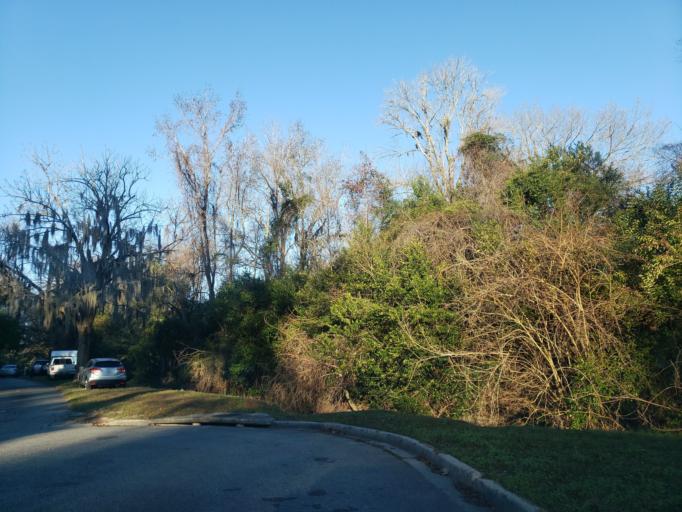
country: US
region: Georgia
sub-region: Chatham County
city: Isle of Hope
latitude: 32.0156
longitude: -81.0999
